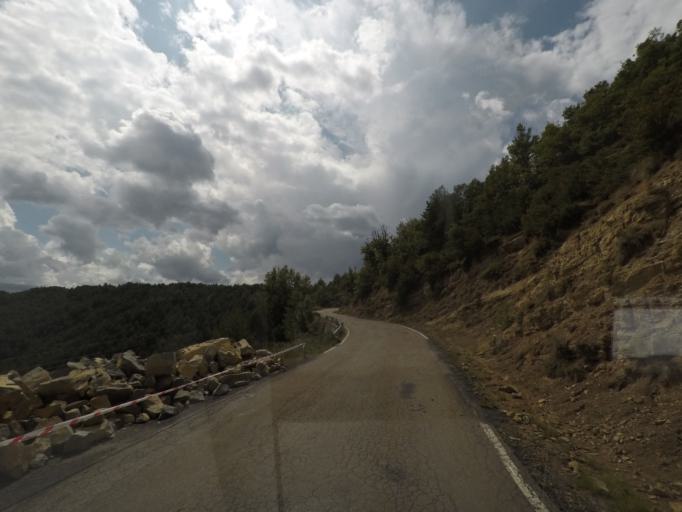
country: ES
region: Aragon
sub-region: Provincia de Huesca
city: Boltana
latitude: 42.4007
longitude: -0.0102
